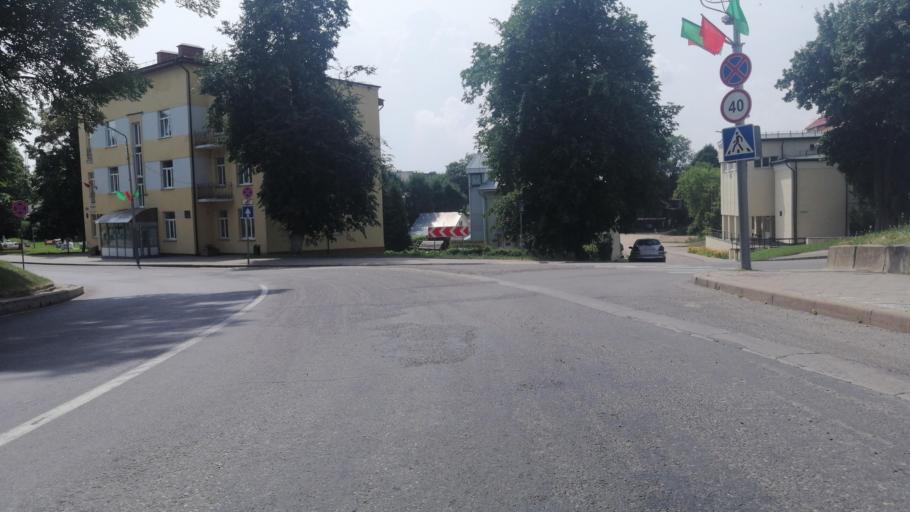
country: BY
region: Grodnenskaya
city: Navahrudak
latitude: 53.5971
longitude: 25.8229
